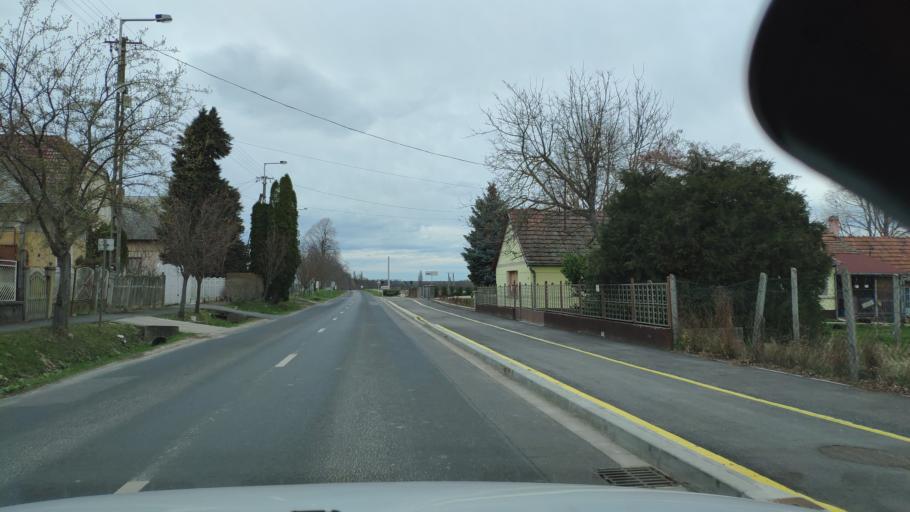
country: HU
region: Zala
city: Zalakomar
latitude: 46.5679
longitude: 17.1241
